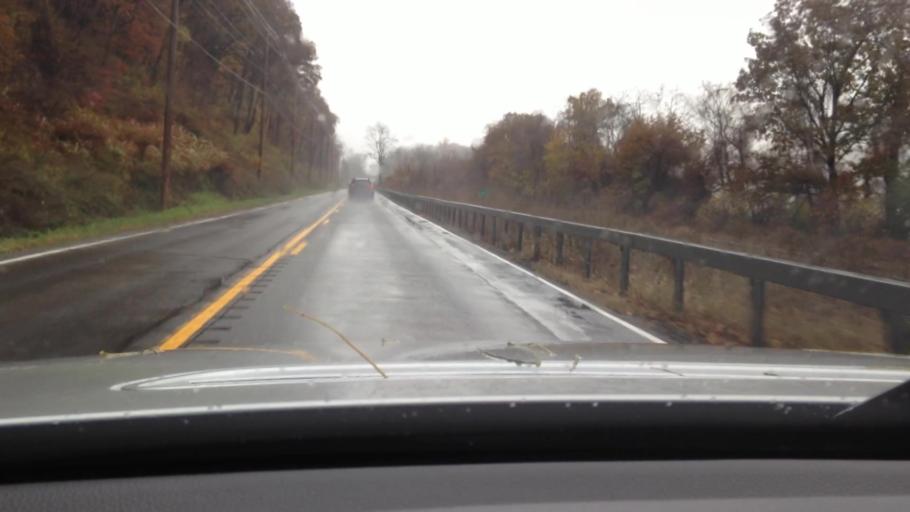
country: US
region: New York
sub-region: Putnam County
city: Cold Spring
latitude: 41.4344
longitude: -73.9707
